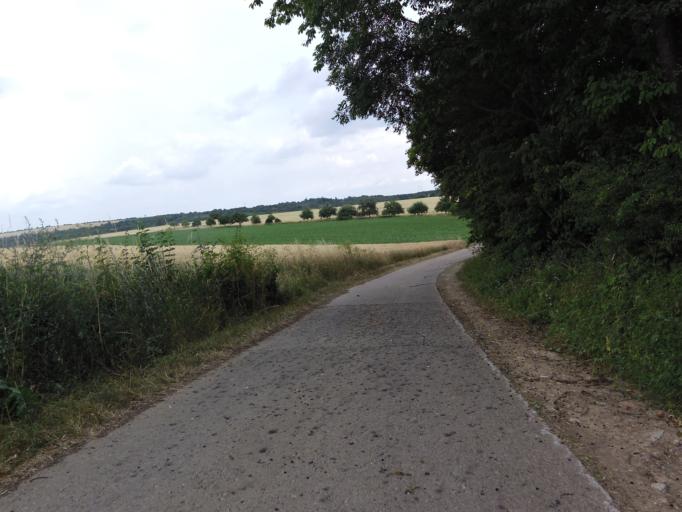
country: DE
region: Bavaria
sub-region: Regierungsbezirk Unterfranken
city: Randersacker
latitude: 49.7696
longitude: 9.9766
